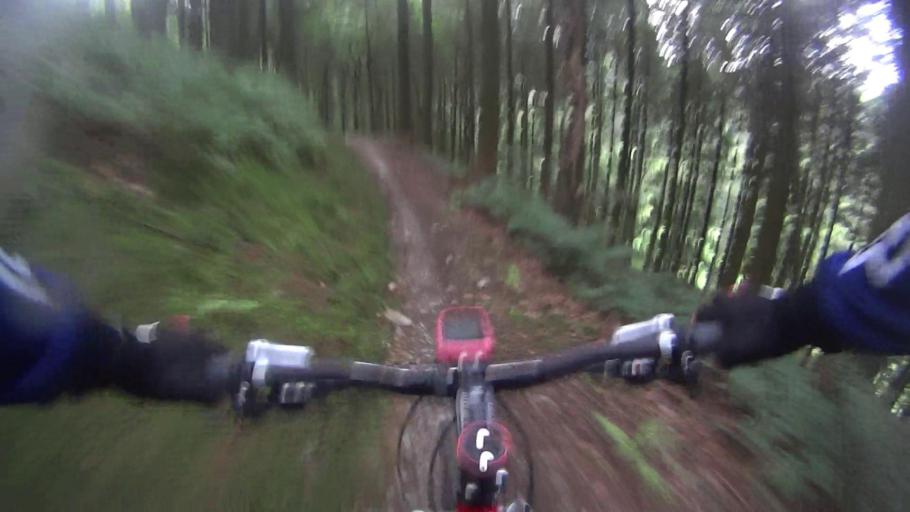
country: GB
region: Wales
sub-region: County of Ceredigion
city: Bow Street
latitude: 52.4185
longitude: -3.9149
